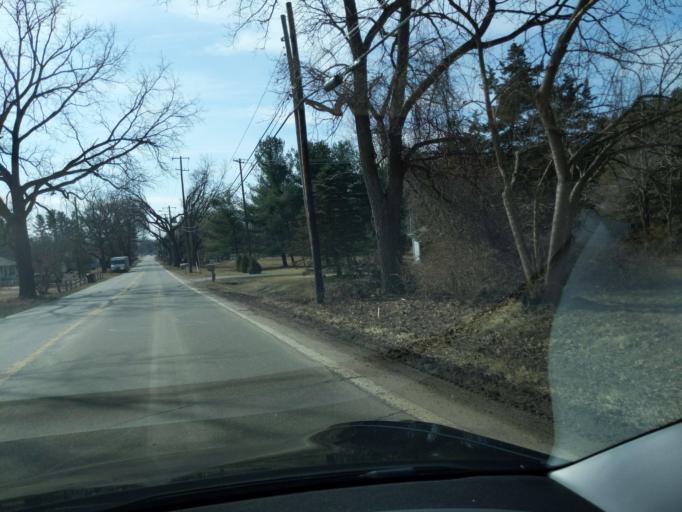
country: US
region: Michigan
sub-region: Ingham County
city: Stockbridge
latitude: 42.4650
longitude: -84.0847
